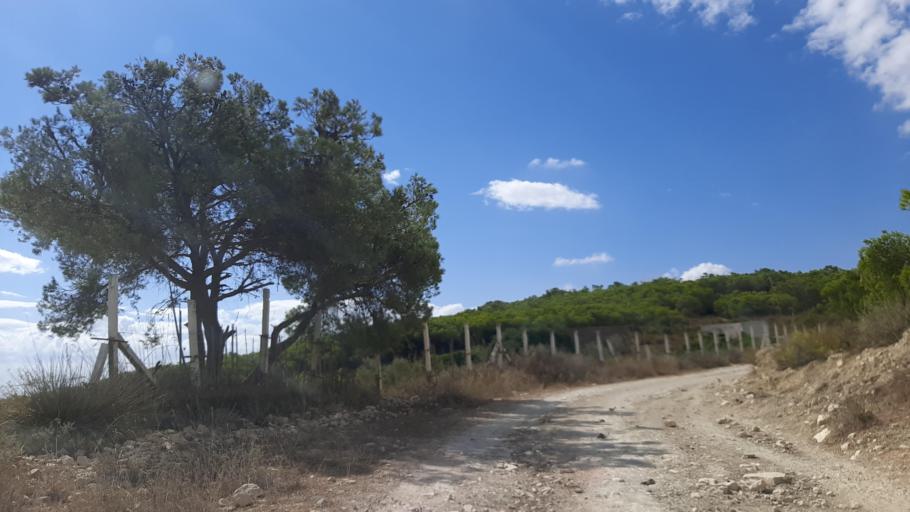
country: TN
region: Zaghwan
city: Zaghouan
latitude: 36.5106
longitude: 10.1841
